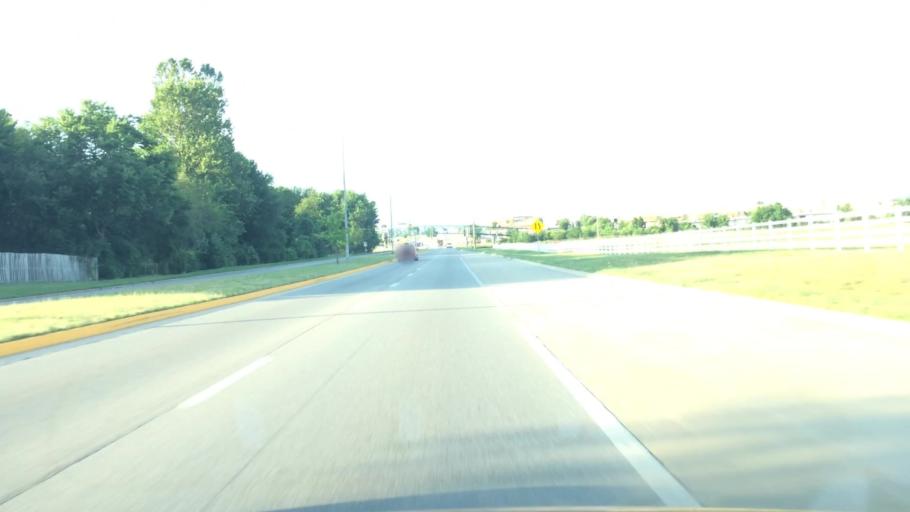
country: US
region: Missouri
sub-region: Greene County
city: Springfield
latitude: 37.1707
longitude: -93.3162
